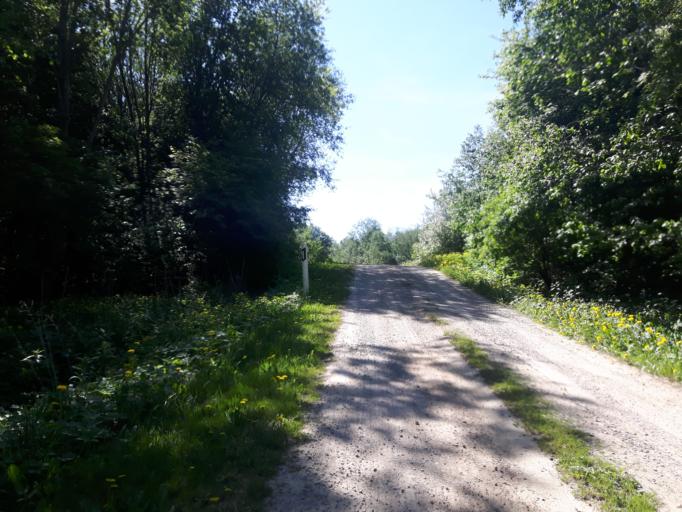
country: EE
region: Ida-Virumaa
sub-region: Kivioli linn
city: Kivioli
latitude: 59.4314
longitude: 26.9531
